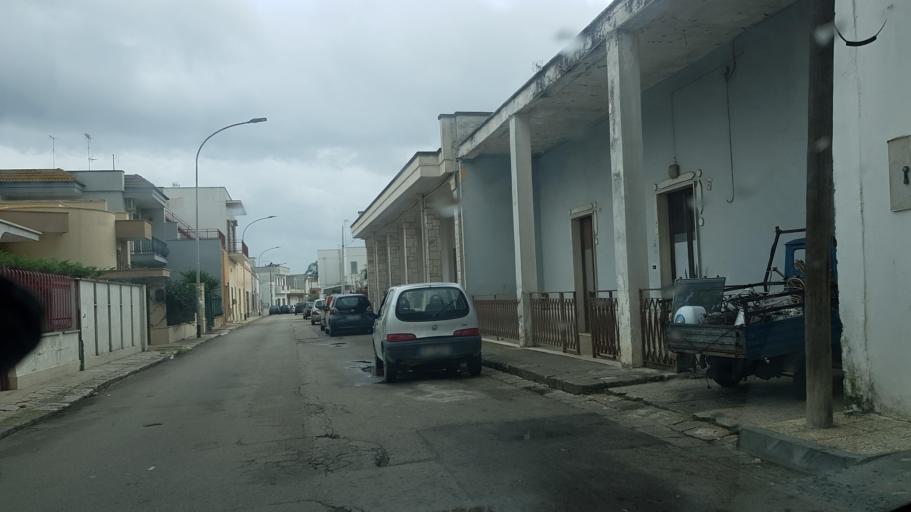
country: IT
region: Apulia
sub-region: Provincia di Lecce
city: Carmiano
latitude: 40.3500
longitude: 18.0466
